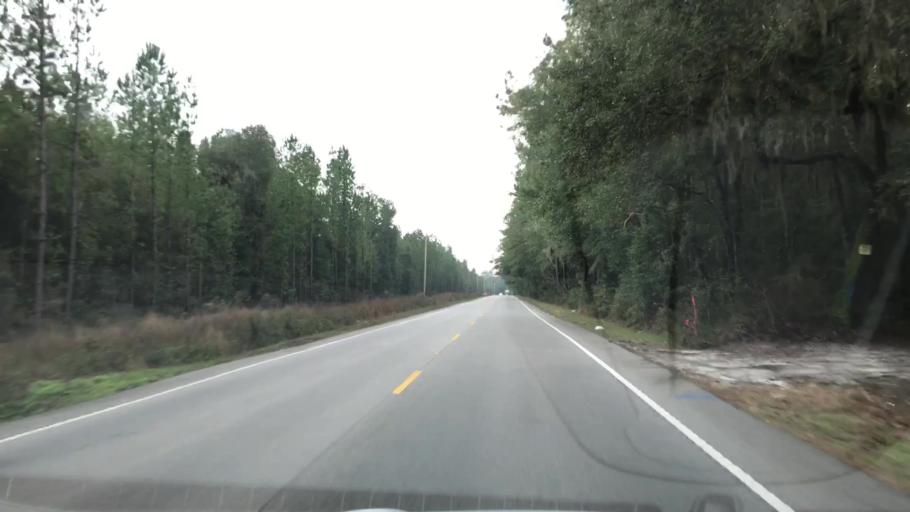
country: US
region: South Carolina
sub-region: Jasper County
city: Ridgeland
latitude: 32.5034
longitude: -80.8866
